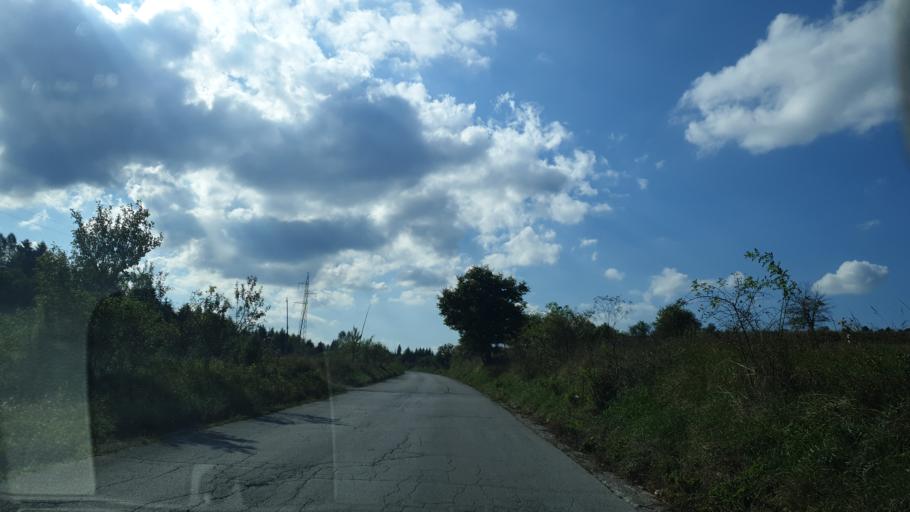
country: RS
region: Central Serbia
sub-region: Zlatiborski Okrug
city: Nova Varos
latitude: 43.4258
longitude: 19.9084
